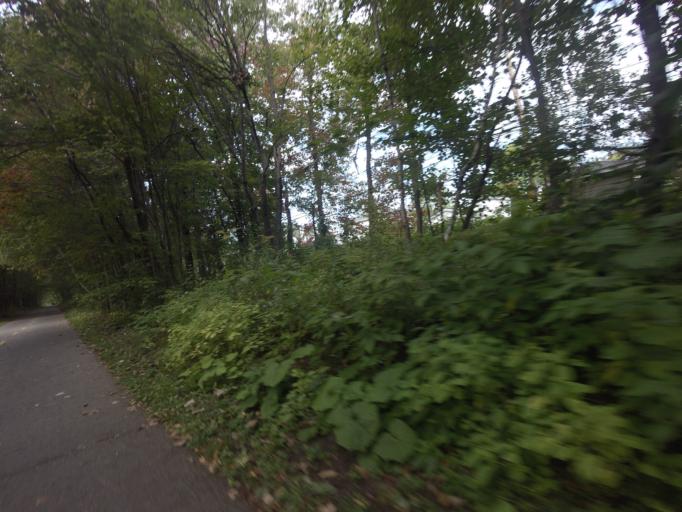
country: CA
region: Quebec
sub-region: Laurentides
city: Blainville
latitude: 45.6930
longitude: -73.8928
